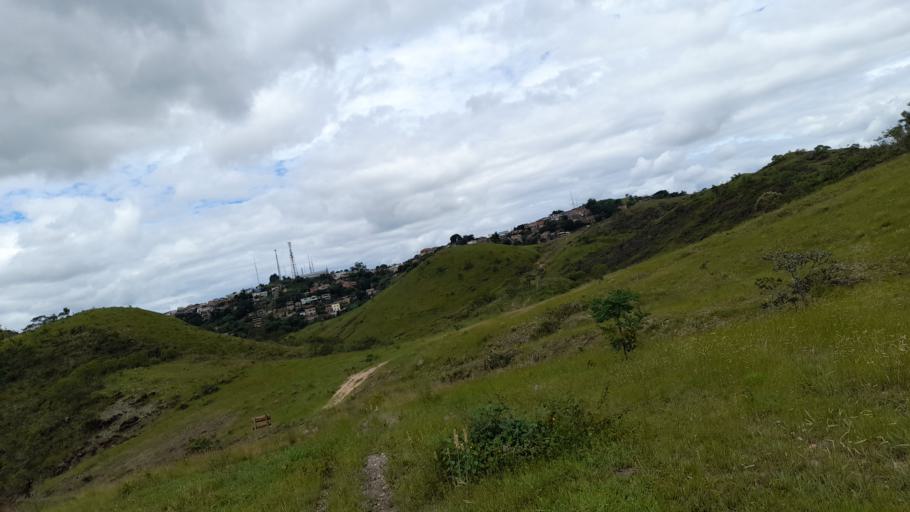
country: BR
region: Minas Gerais
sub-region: Sao Joao Del Rei
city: Sao Joao del Rei
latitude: -21.1248
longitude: -44.2741
